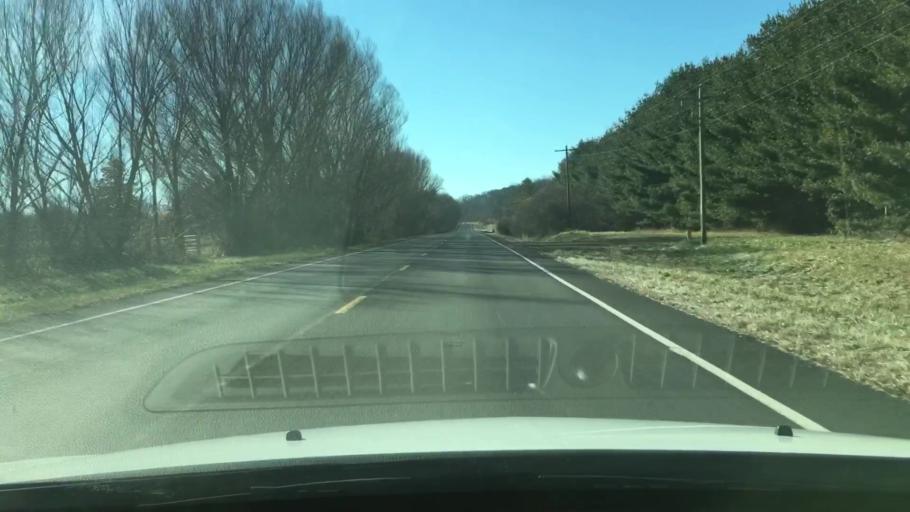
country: US
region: Illinois
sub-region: Fulton County
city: Canton
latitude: 40.4924
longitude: -89.9385
